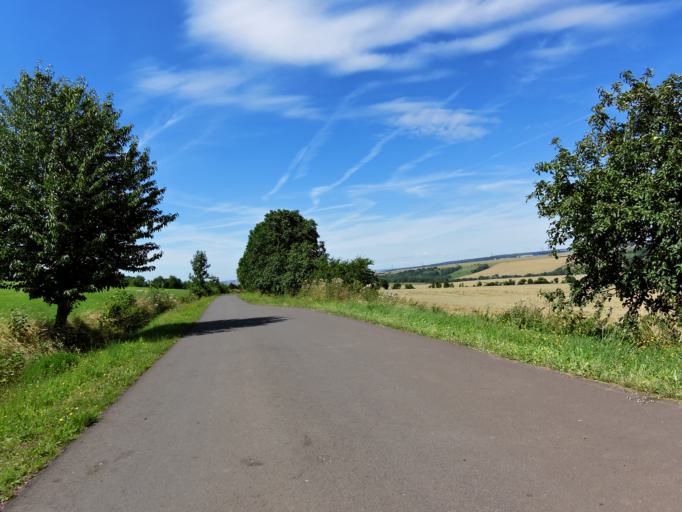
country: DE
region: Thuringia
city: Haina
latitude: 50.9627
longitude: 10.4750
